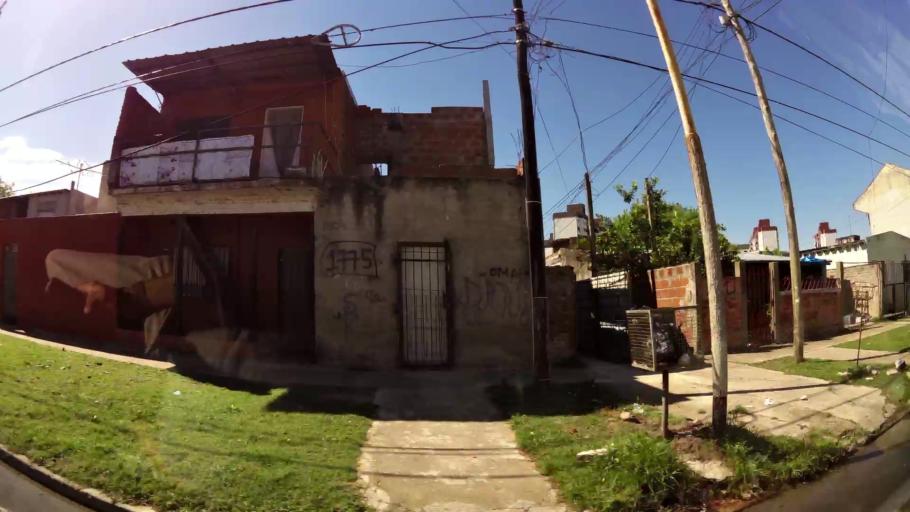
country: AR
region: Buenos Aires
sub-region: Partido de Quilmes
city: Quilmes
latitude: -34.6893
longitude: -58.3023
